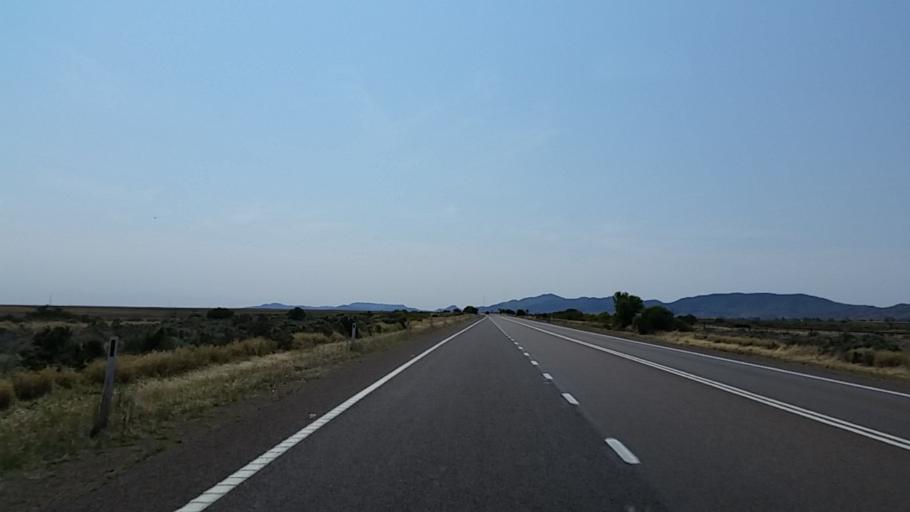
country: AU
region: South Australia
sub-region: Port Augusta
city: Port Augusta
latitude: -32.7108
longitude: 137.9410
